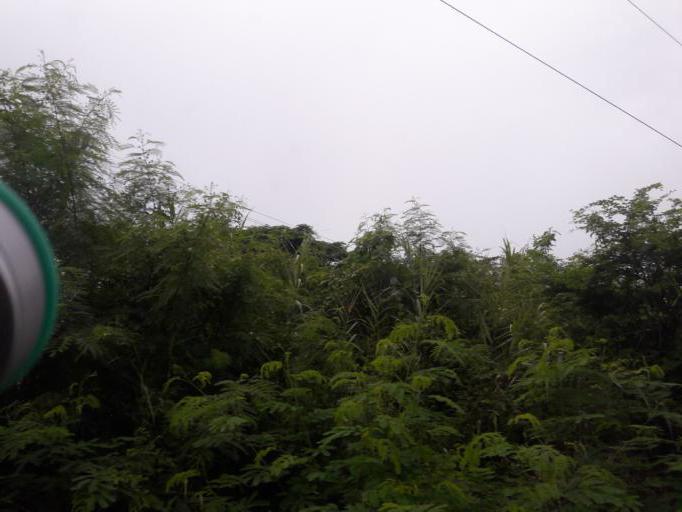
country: TH
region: Ratchaburi
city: Damnoen Saduak
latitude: 13.5069
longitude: 100.0243
